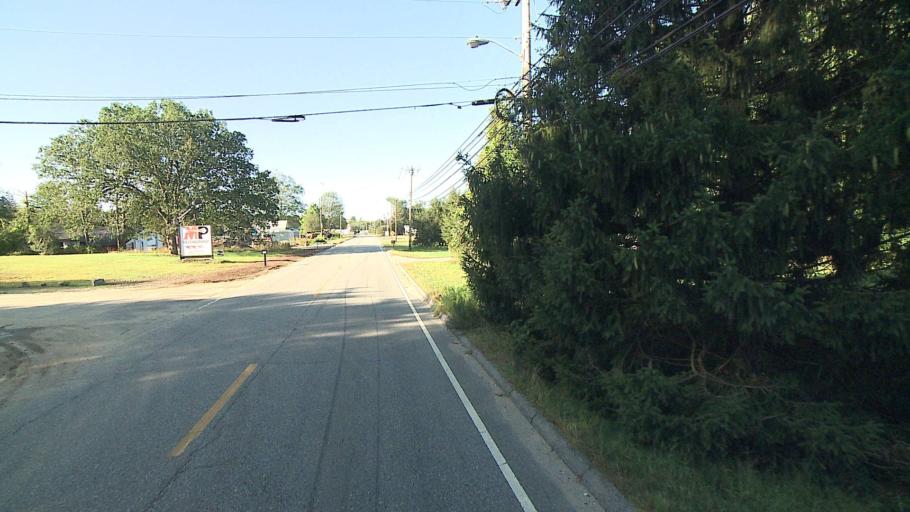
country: US
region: Connecticut
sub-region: Windham County
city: Plainfield Village
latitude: 41.6590
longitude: -71.9262
